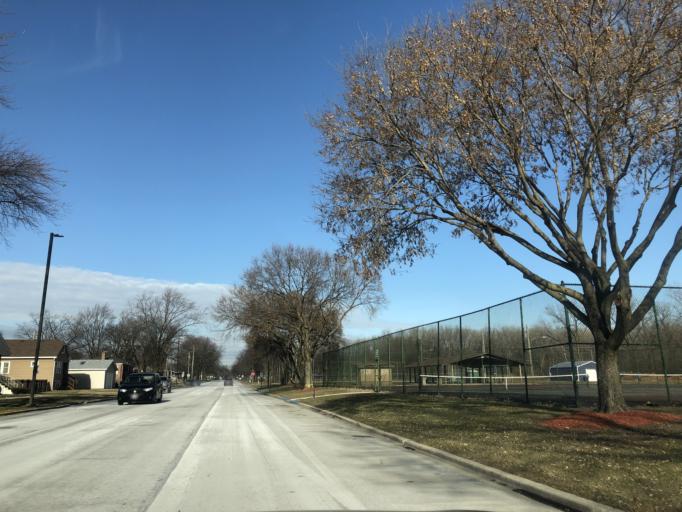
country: US
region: Illinois
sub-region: Cook County
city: Stickney
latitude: 41.8164
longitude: -87.7826
